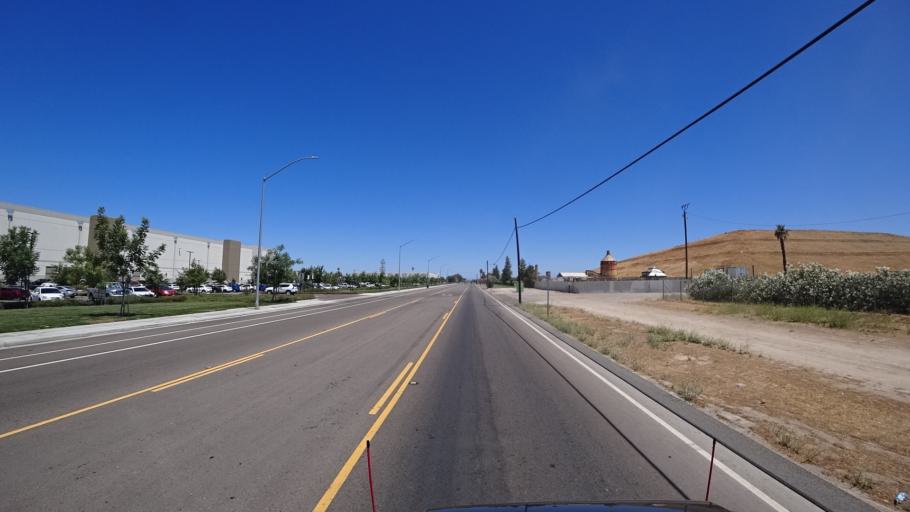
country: US
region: California
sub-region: Fresno County
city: Easton
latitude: 36.6843
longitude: -119.7636
